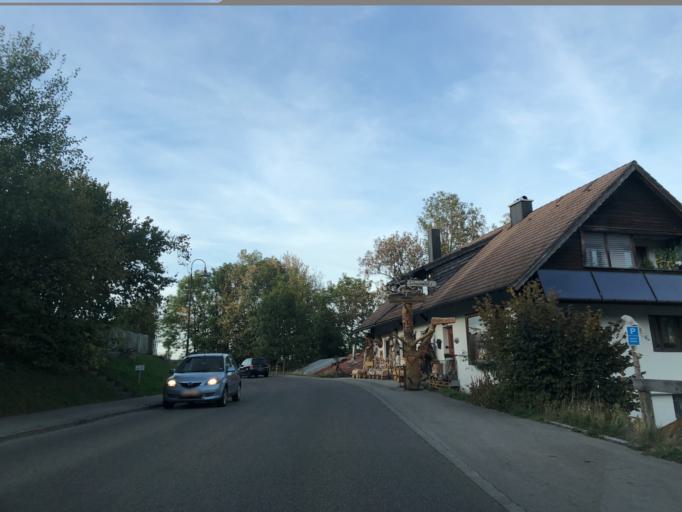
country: DE
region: Bavaria
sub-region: Swabia
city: Pfronten
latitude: 47.5869
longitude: 10.5596
